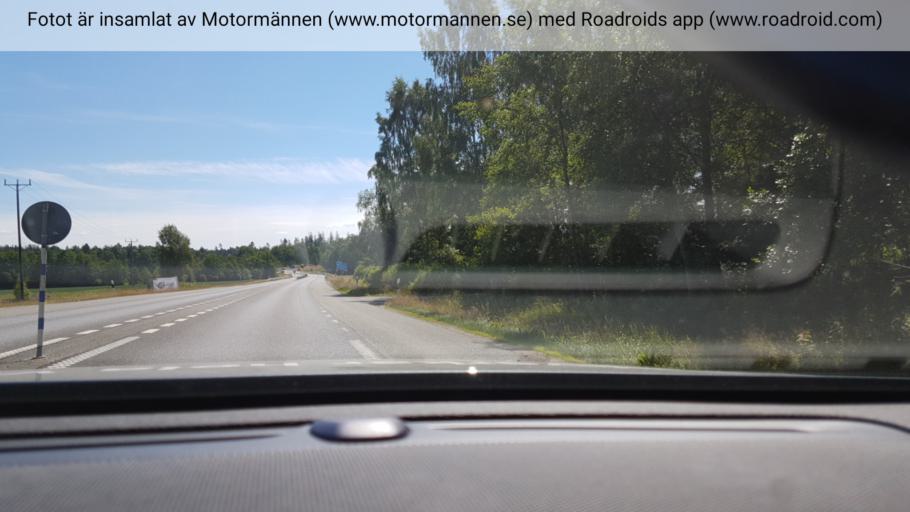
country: SE
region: Kronoberg
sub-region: Ljungby Kommun
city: Ljungby
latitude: 56.8522
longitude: 13.9678
